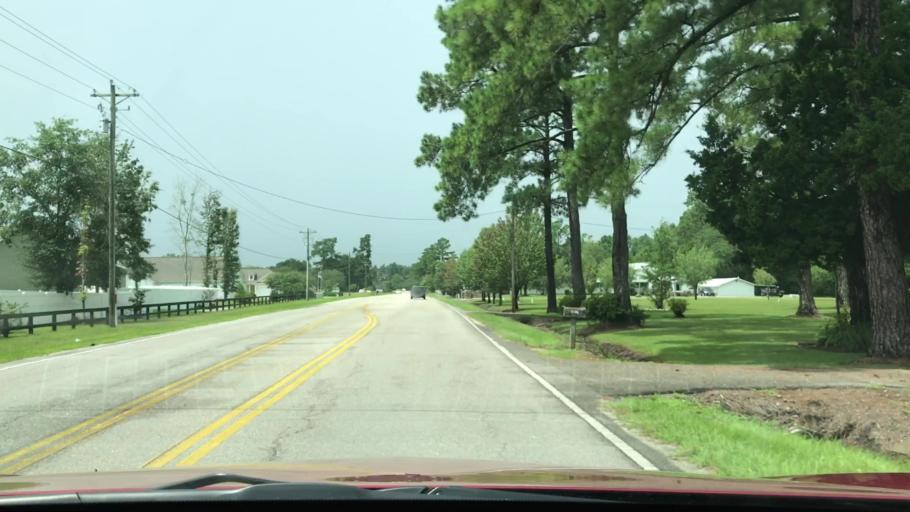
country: US
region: South Carolina
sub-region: Horry County
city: Red Hill
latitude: 33.8893
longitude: -78.9535
